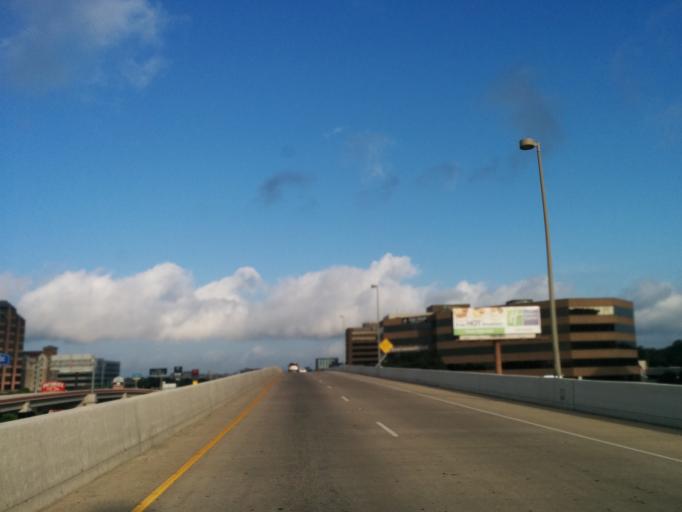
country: US
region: Texas
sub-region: Bexar County
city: Castle Hills
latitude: 29.5206
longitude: -98.4855
